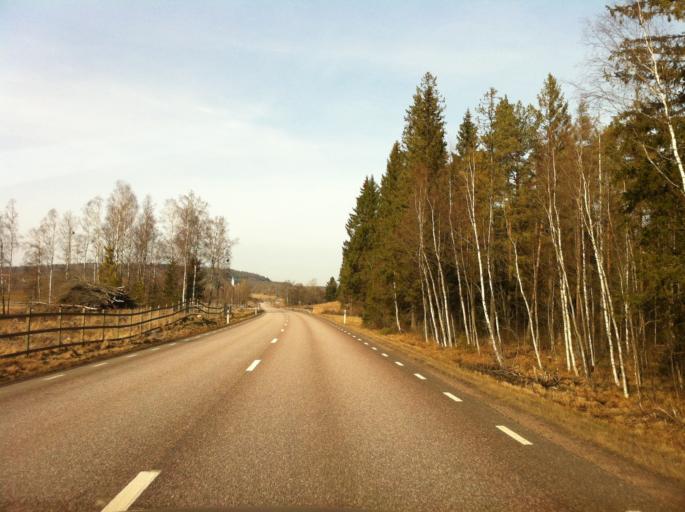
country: SE
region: Vaestra Goetaland
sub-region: Skovde Kommun
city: Skultorp
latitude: 58.2780
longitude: 13.8096
